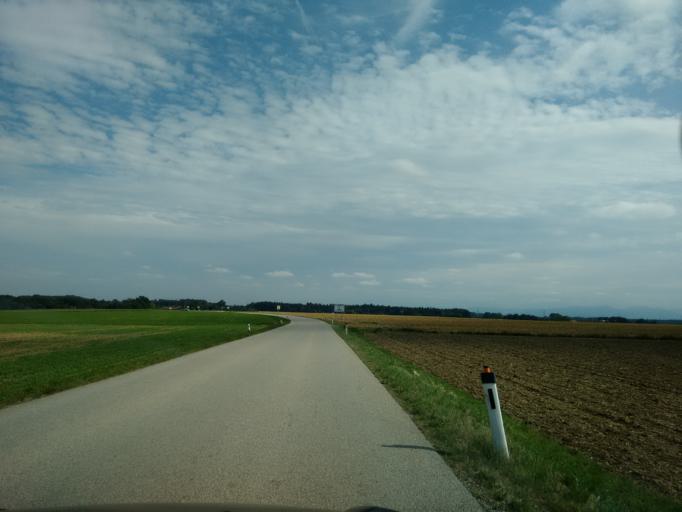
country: AT
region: Upper Austria
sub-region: Wels-Land
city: Marchtrenk
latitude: 48.1205
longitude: 14.1241
